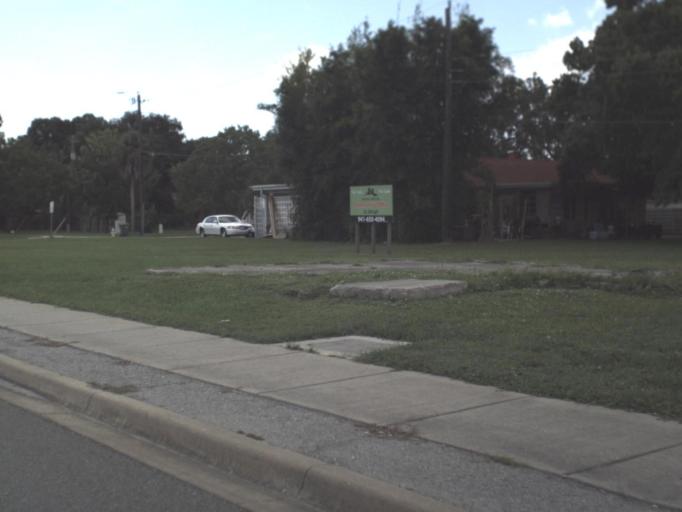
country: US
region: Florida
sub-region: Sarasota County
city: Sarasota
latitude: 27.3377
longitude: -82.5153
